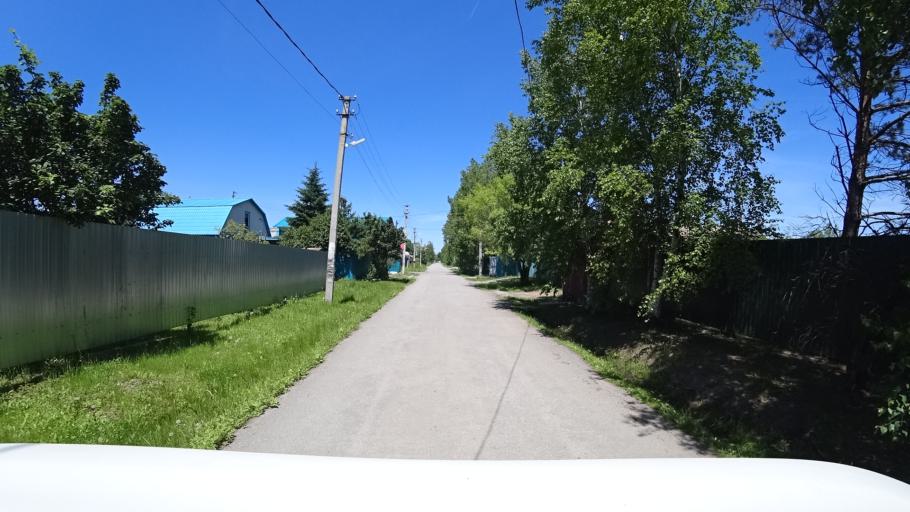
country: RU
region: Khabarovsk Krai
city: Topolevo
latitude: 48.5099
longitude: 135.1758
